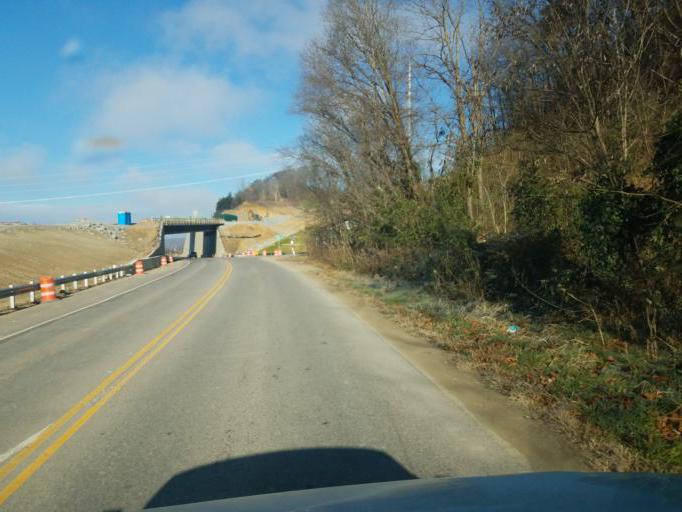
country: US
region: Ohio
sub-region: Scioto County
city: Sciotodale
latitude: 38.7472
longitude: -82.8709
